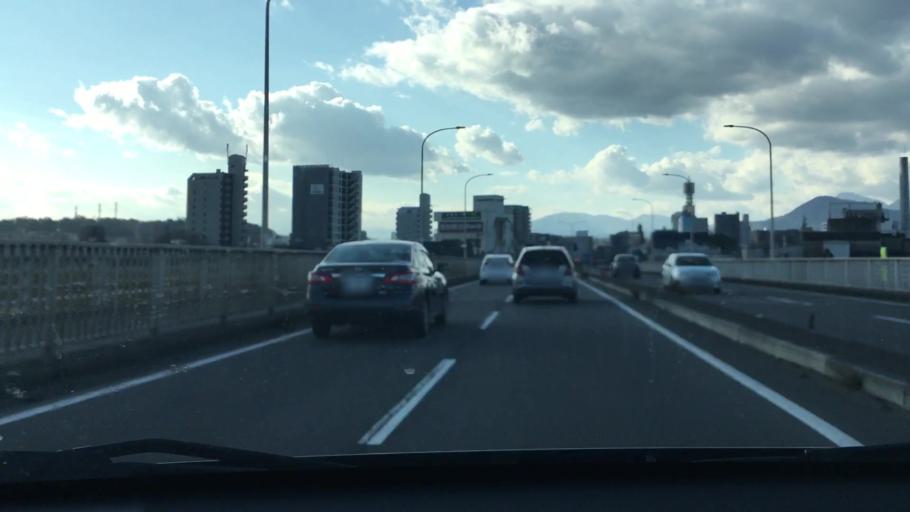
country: JP
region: Oita
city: Oita
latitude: 33.2320
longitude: 131.6240
